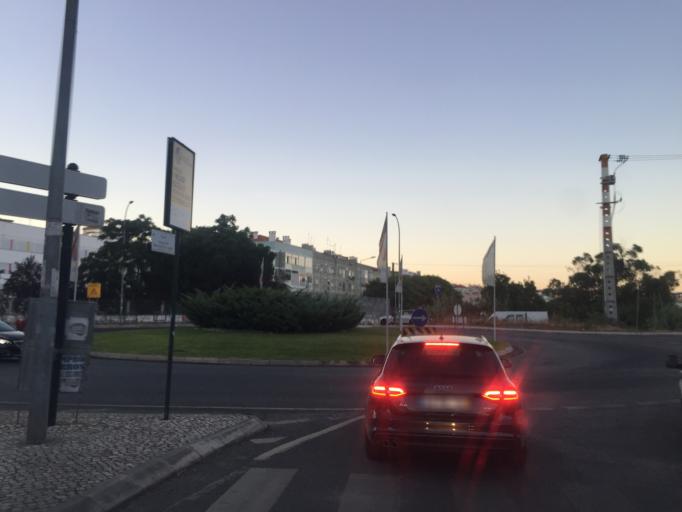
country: PT
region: Lisbon
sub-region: Odivelas
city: Olival do Basto
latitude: 38.7891
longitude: -9.1745
